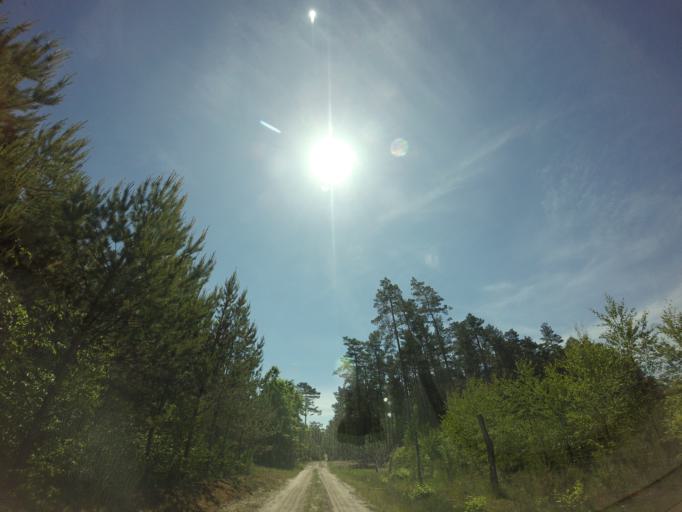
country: PL
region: West Pomeranian Voivodeship
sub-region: Powiat choszczenski
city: Drawno
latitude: 53.2534
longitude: 15.7500
